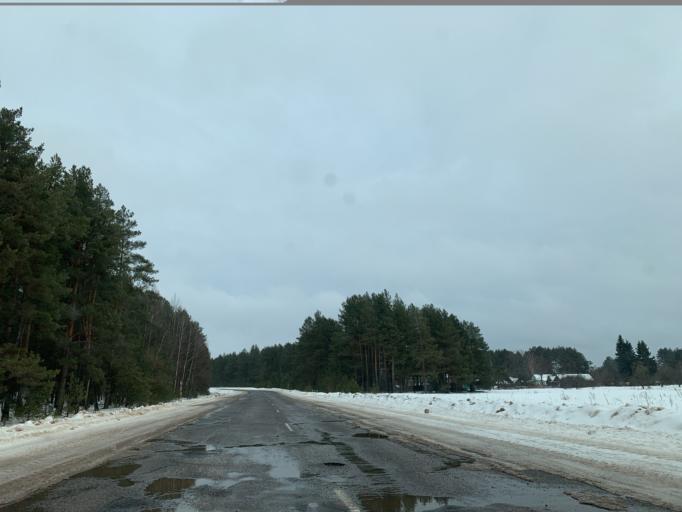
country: BY
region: Minsk
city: Il'ya
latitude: 54.3278
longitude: 27.2508
